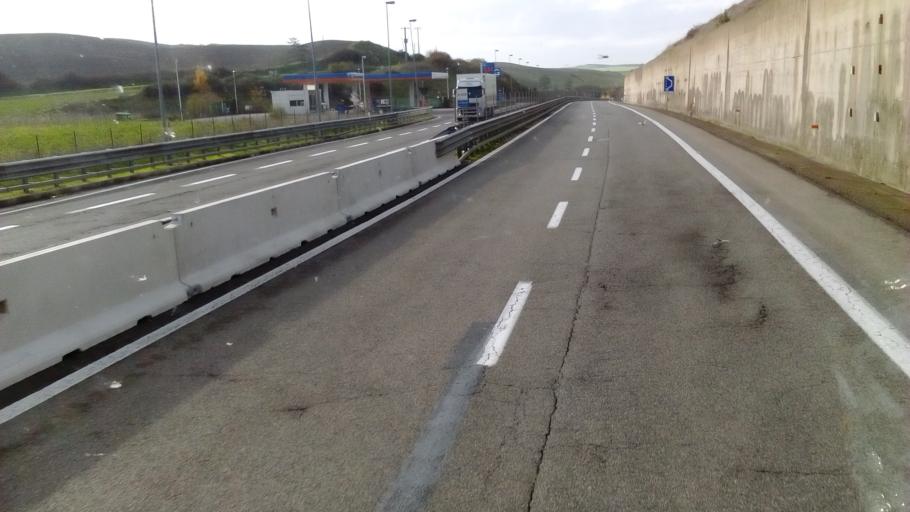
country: IT
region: Tuscany
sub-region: Provincia di Siena
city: Castelnuovo Berardenga
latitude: 43.3169
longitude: 11.4769
